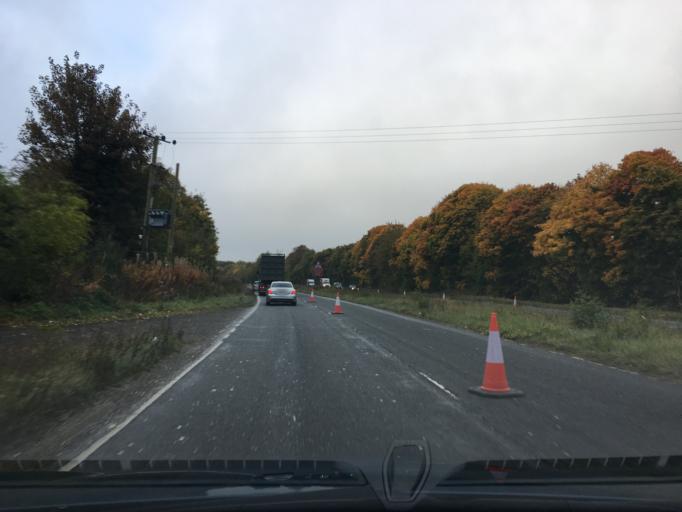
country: GB
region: England
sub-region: Hampshire
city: Alton
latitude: 51.1363
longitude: -0.9876
